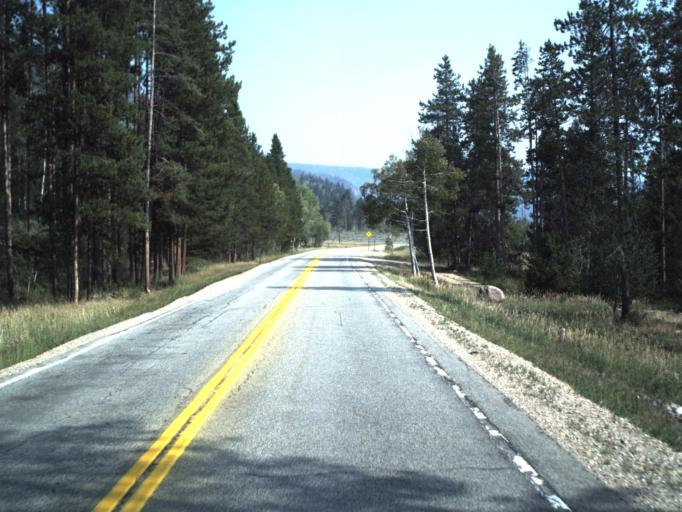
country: US
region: Utah
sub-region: Summit County
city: Francis
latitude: 40.5948
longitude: -111.0753
